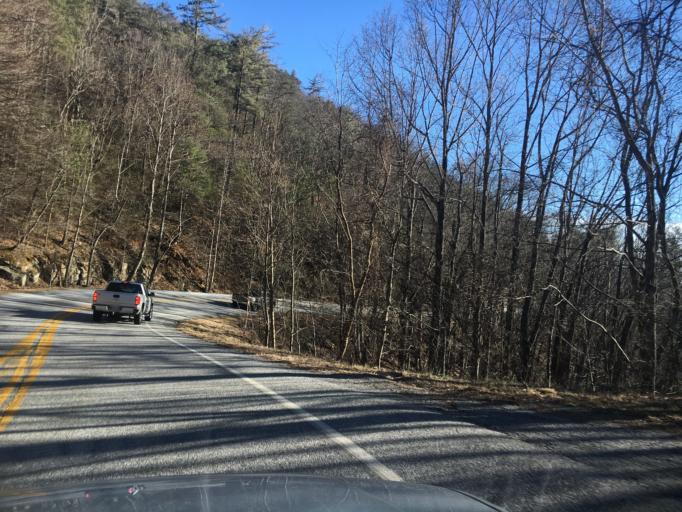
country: US
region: Georgia
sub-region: Union County
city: Blairsville
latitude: 34.7266
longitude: -83.9134
